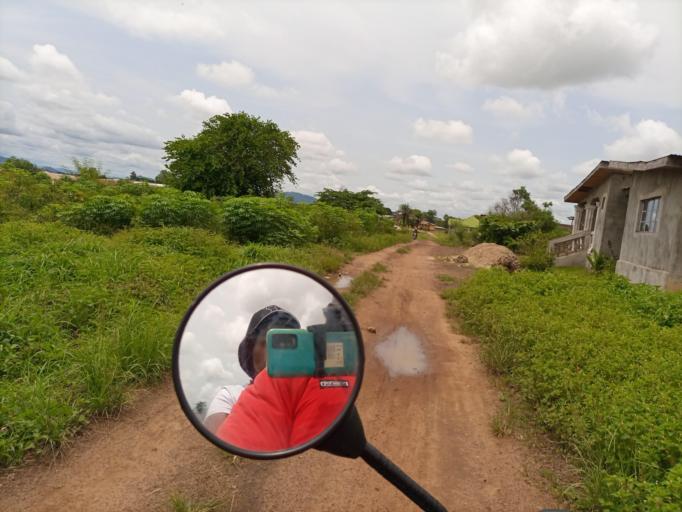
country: SL
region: Southern Province
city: Baoma
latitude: 7.9769
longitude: -11.7194
